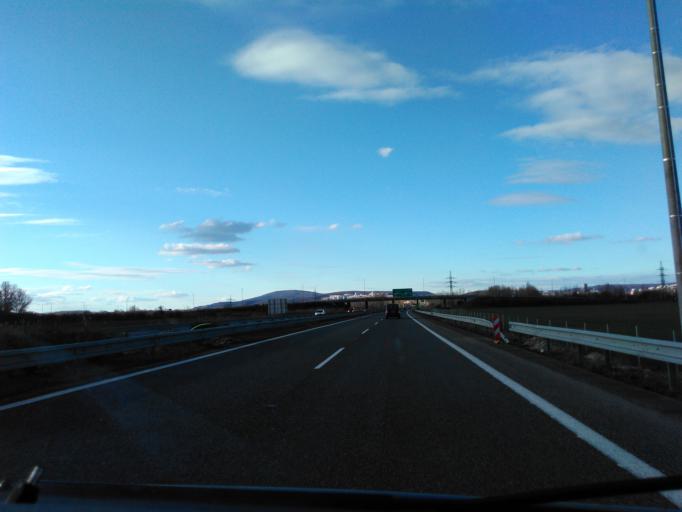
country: AT
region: Burgenland
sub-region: Politischer Bezirk Neusiedl am See
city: Kittsee
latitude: 48.1136
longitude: 17.0829
